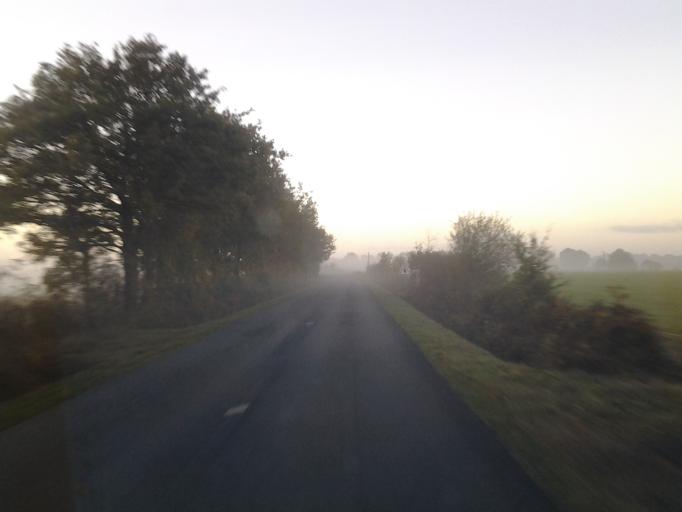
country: FR
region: Pays de la Loire
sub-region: Departement de la Vendee
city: Bournezeau
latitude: 46.6455
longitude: -1.2313
